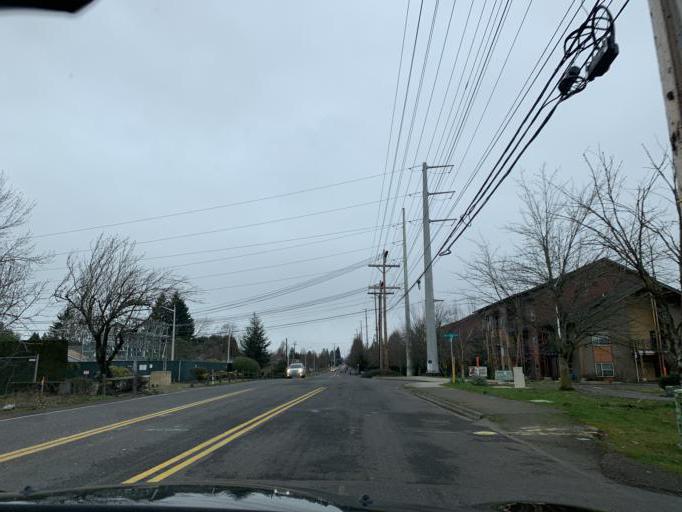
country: US
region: Washington
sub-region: Clark County
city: Mill Plain
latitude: 45.6212
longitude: -122.5019
